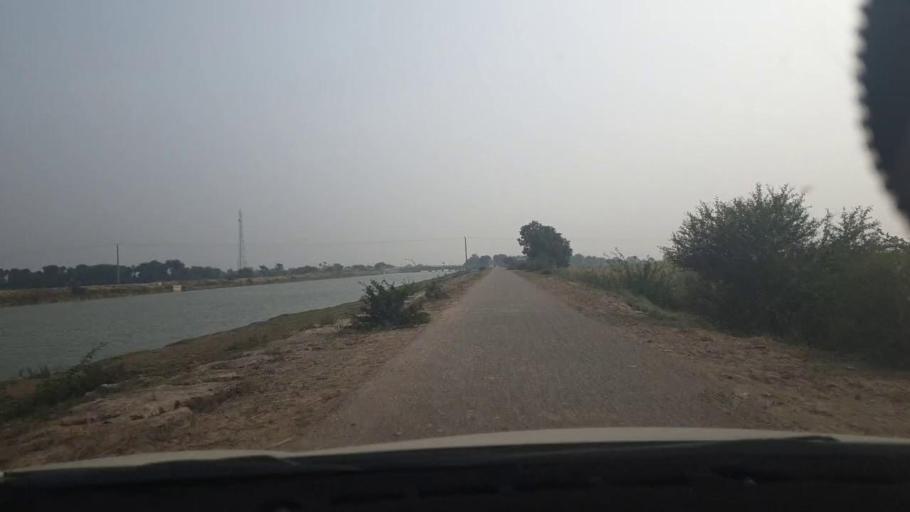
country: PK
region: Sindh
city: Tando Muhammad Khan
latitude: 24.9637
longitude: 68.4955
